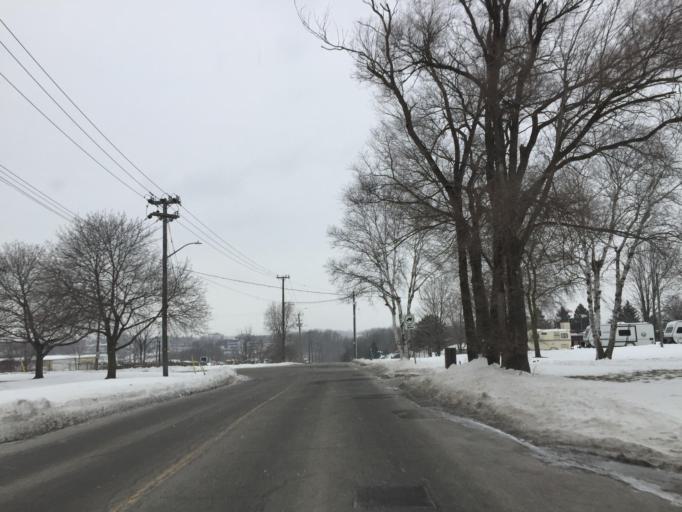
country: CA
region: Ontario
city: Waterloo
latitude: 43.4690
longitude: -80.4698
